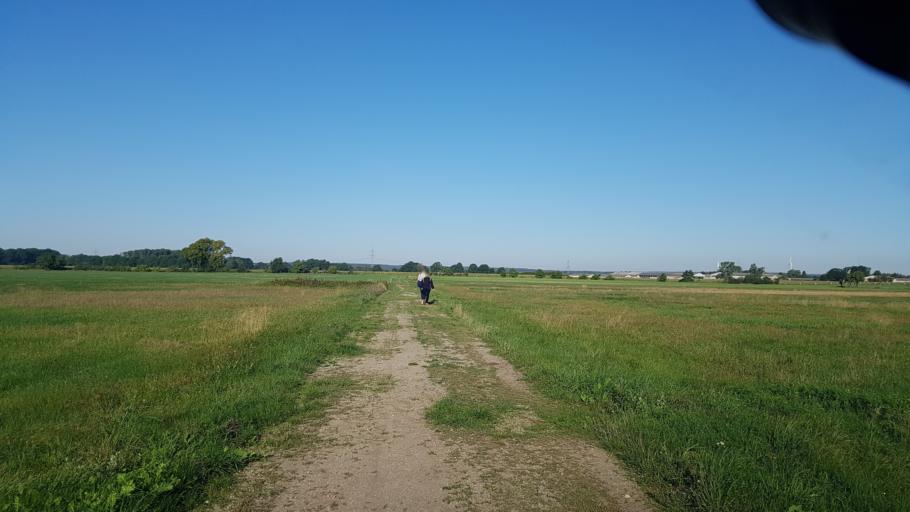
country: DE
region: Brandenburg
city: Ruckersdorf
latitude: 51.5838
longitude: 13.5488
